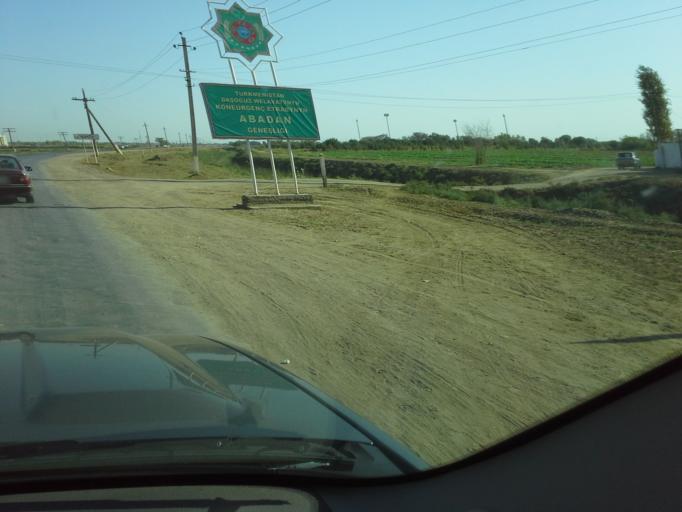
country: TM
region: Dasoguz
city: Koeneuergench
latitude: 42.3398
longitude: 59.1589
